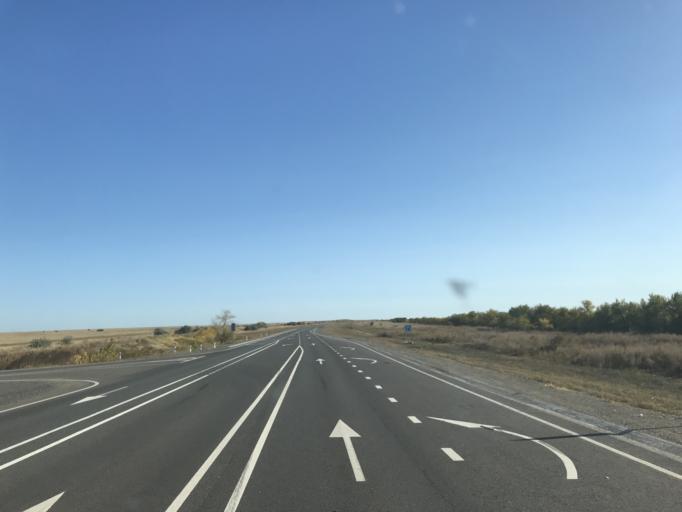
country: KZ
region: Pavlodar
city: Aksu
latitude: 52.0151
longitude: 77.2374
